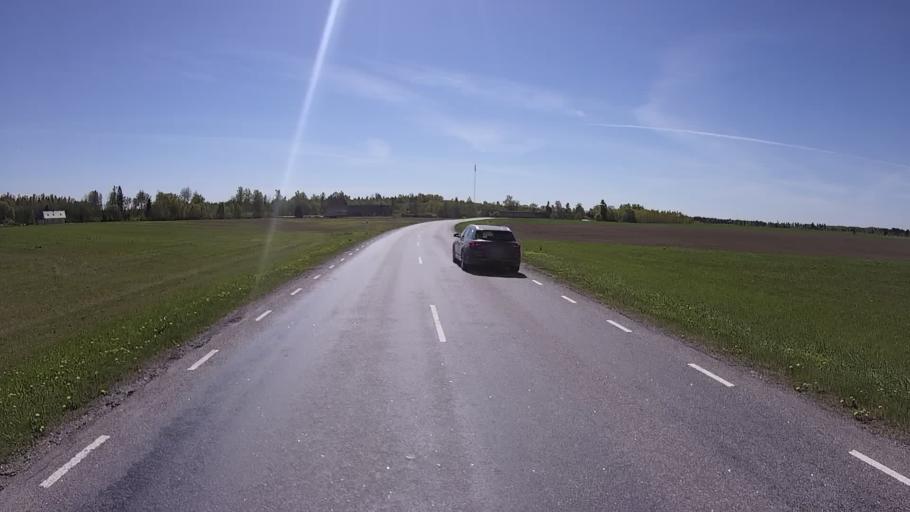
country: EE
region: Harju
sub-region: Raasiku vald
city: Raasiku
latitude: 59.0752
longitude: 25.1639
